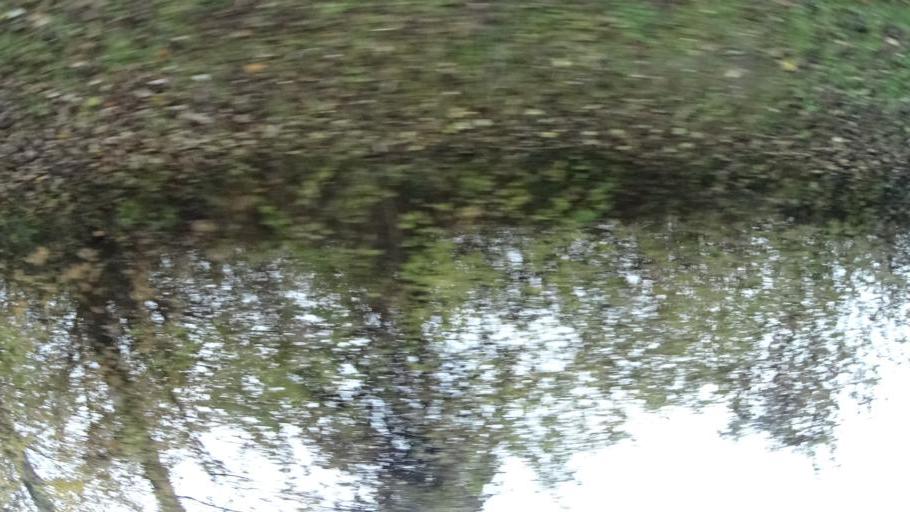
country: DE
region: Baden-Wuerttemberg
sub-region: Karlsruhe Region
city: Sinzheim
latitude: 48.7535
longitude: 8.1772
